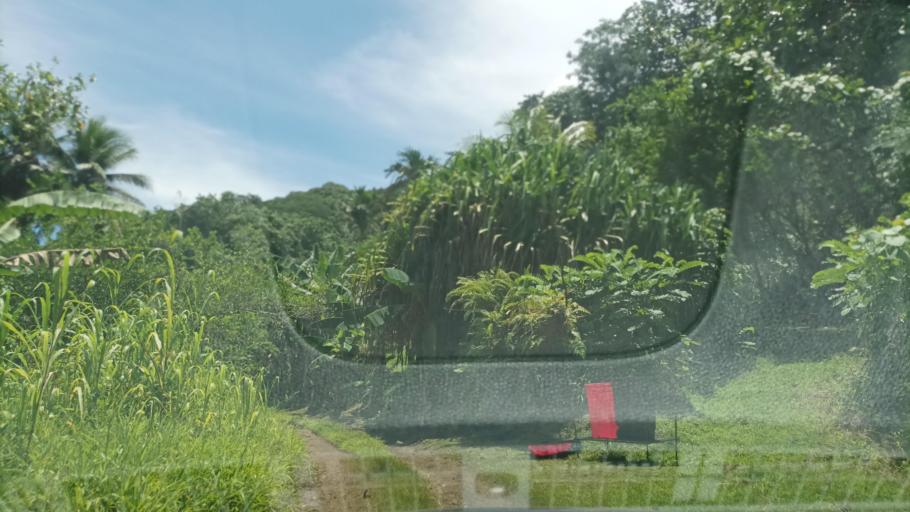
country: FM
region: Kosrae
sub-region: Malem Municipality
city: Malem
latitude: 5.2961
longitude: 163.0237
